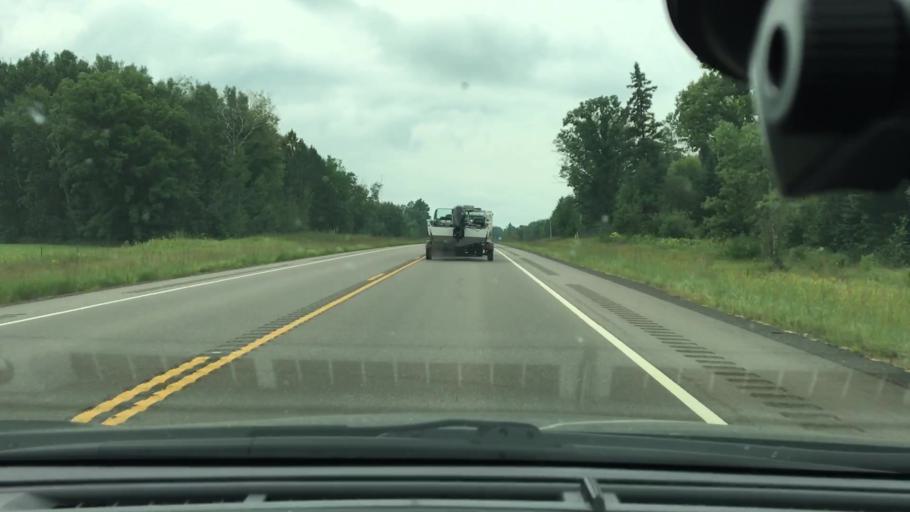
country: US
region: Minnesota
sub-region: Crow Wing County
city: Crosby
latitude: 46.5761
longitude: -93.9527
